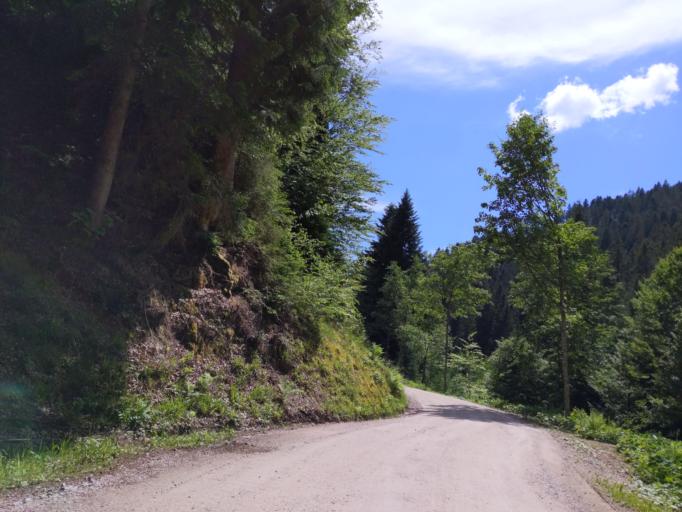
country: DE
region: Baden-Wuerttemberg
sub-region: Karlsruhe Region
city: Bad Rippoldsau-Schapbach
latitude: 48.4210
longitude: 8.3637
